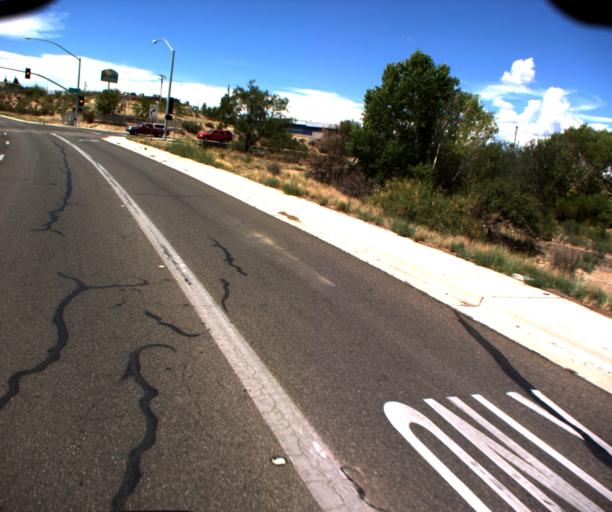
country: US
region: Arizona
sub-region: Yavapai County
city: Camp Verde
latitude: 34.5565
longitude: -111.8547
